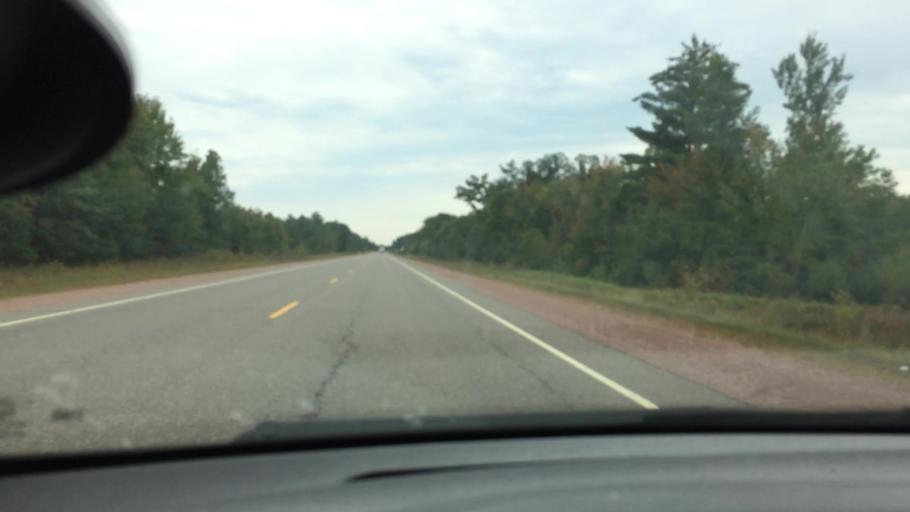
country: US
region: Wisconsin
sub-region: Clark County
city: Neillsville
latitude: 44.5654
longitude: -90.7044
